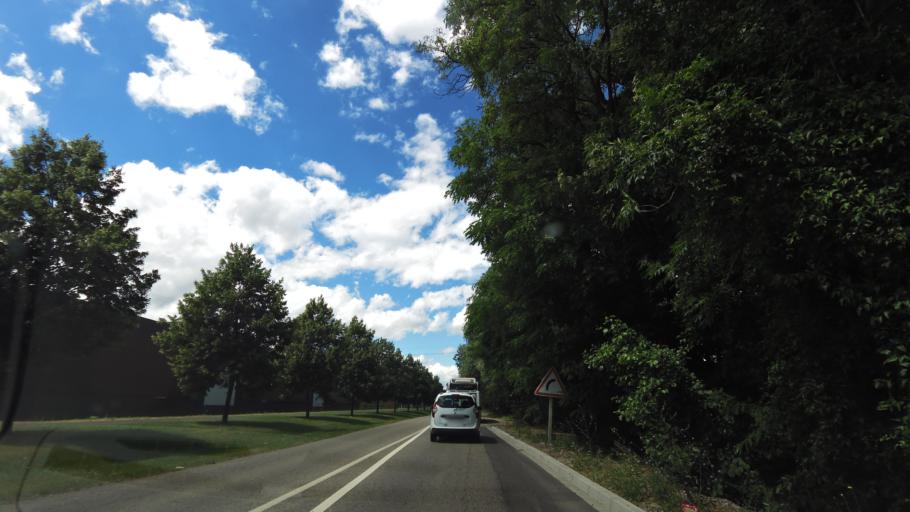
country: FR
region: Alsace
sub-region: Departement du Bas-Rhin
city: Illkirch-Graffenstaden
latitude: 48.5256
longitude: 7.6894
